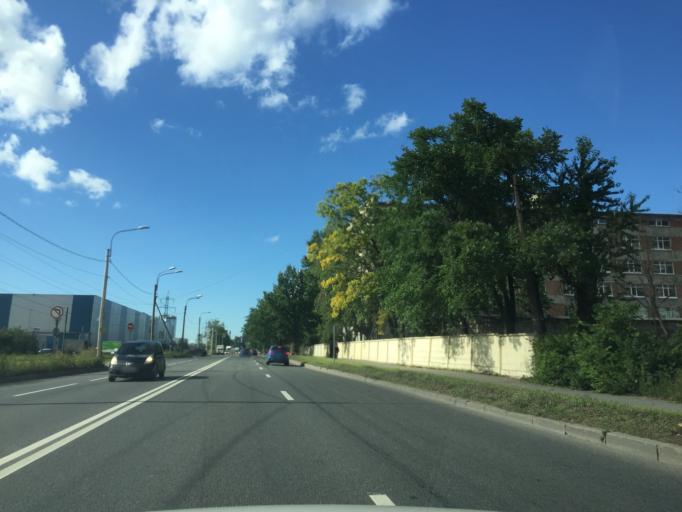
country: RU
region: St.-Petersburg
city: Dachnoye
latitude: 59.8405
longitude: 30.2998
